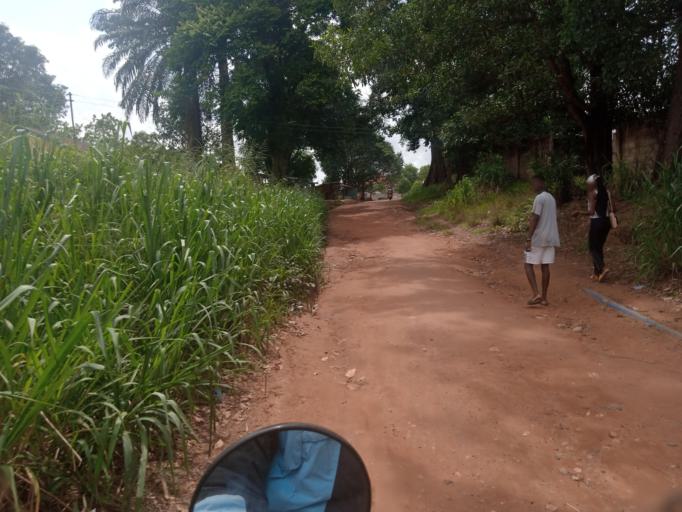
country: SL
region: Southern Province
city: Bo
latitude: 7.9640
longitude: -11.7472
